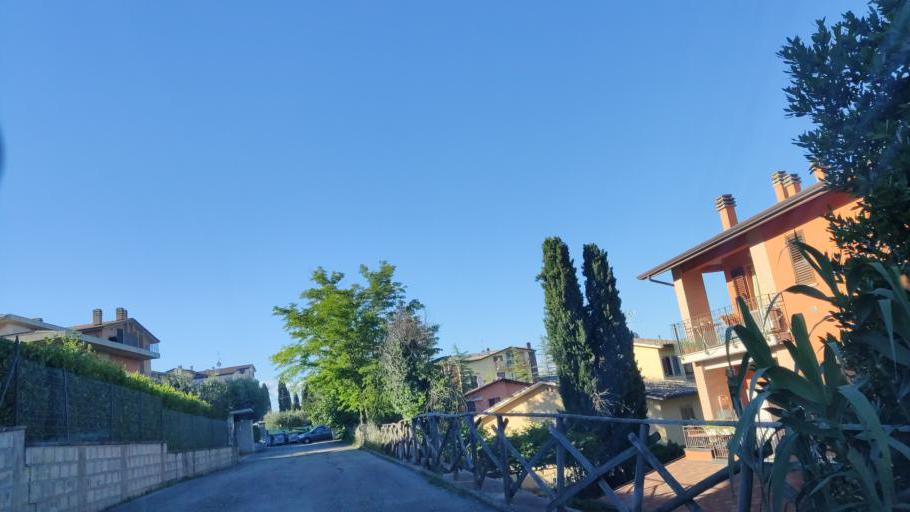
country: IT
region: Umbria
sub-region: Provincia di Perugia
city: Via Lippia
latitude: 43.1038
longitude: 12.4924
